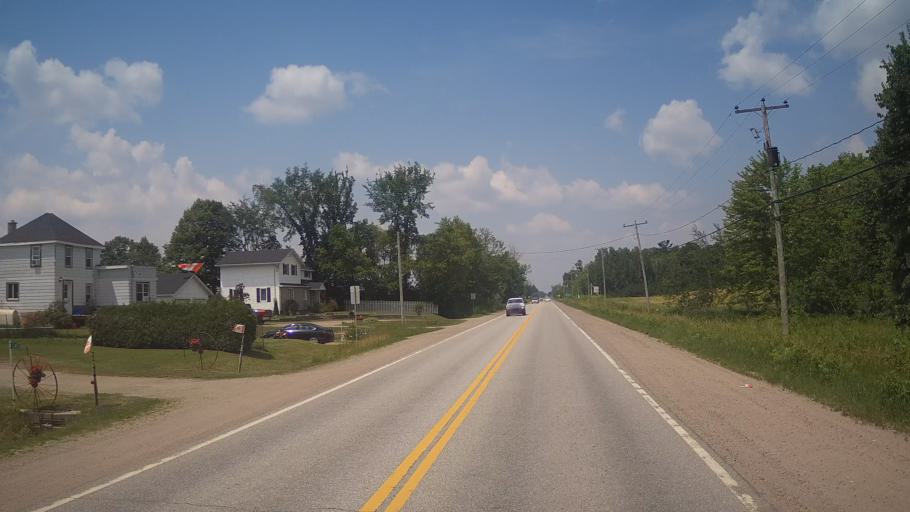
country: CA
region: Quebec
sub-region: Outaouais
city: Shawville
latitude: 45.6007
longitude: -76.4964
